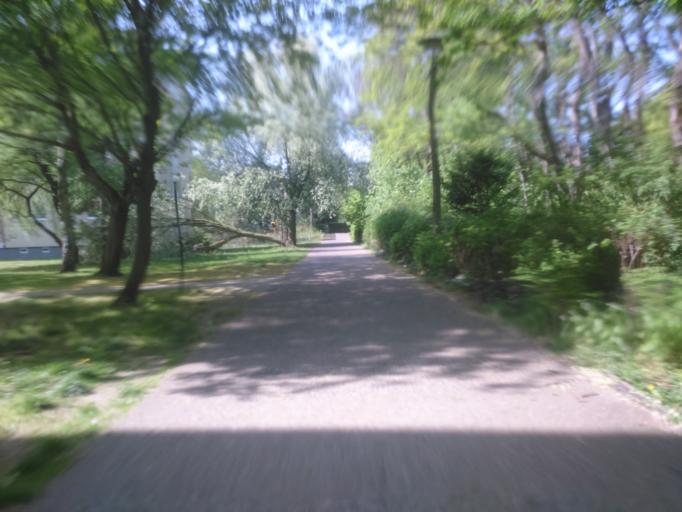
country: DE
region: Berlin
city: Weissensee
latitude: 52.5430
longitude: 13.4564
